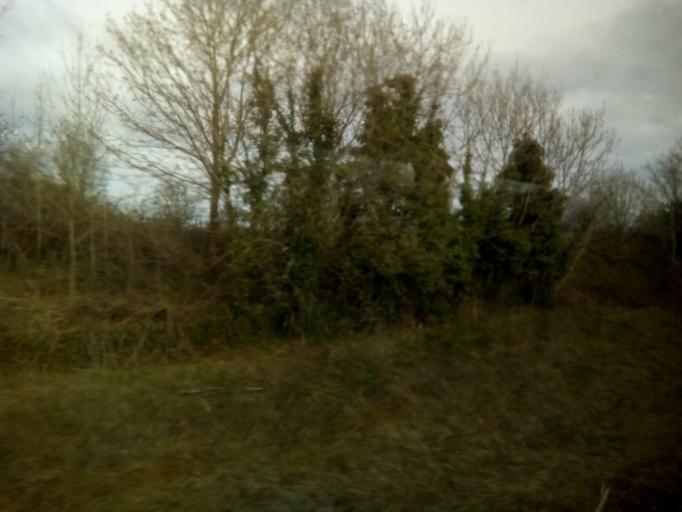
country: IE
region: Leinster
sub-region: Kildare
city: Kilcock
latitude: 53.4071
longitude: -6.6824
